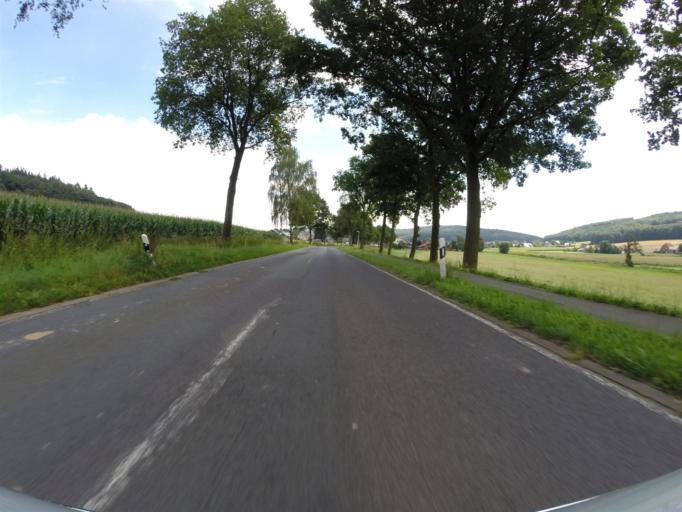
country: DE
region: North Rhine-Westphalia
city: Preussisch Oldendorf
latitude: 52.2736
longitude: 8.5161
